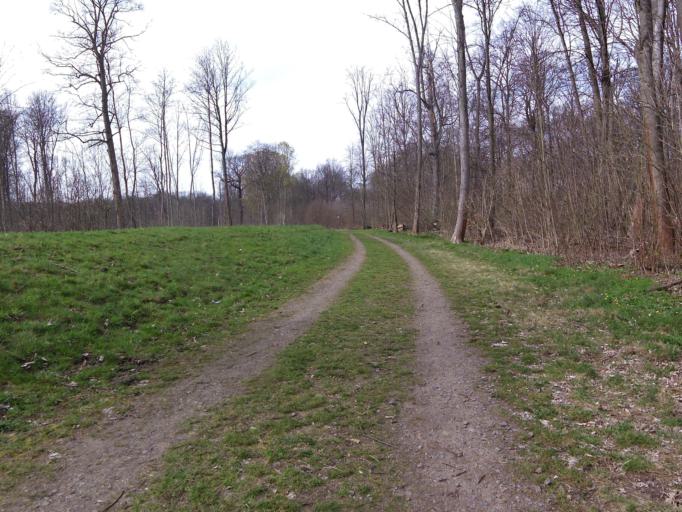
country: DE
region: Saxony
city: Leipzig
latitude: 51.3541
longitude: 12.3322
